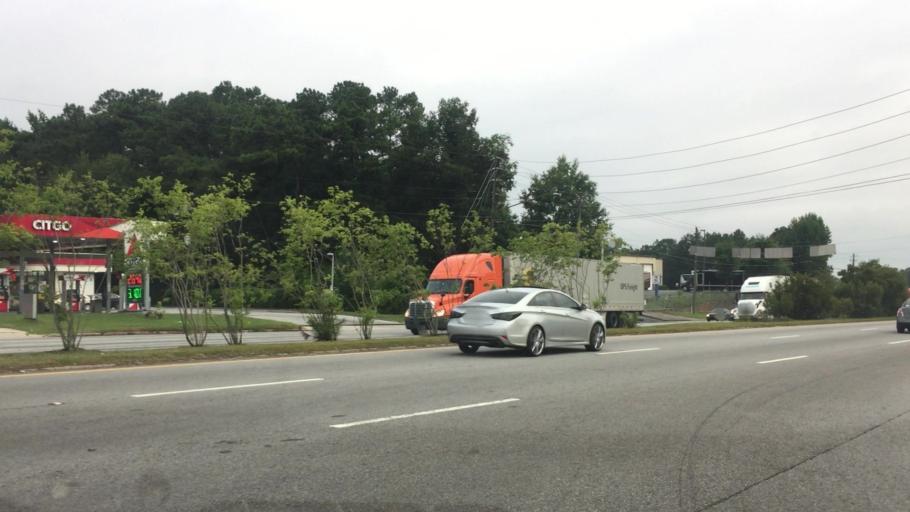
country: US
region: Georgia
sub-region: Clayton County
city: Conley
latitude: 33.6688
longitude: -84.3402
